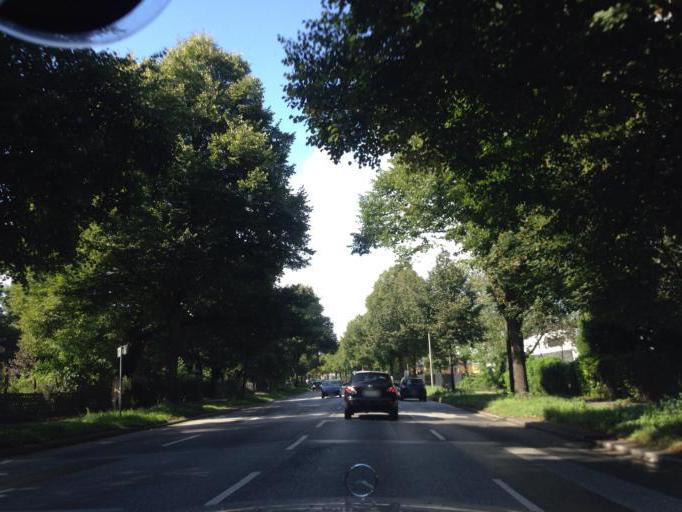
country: DE
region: Hamburg
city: Steilshoop
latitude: 53.5879
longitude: 10.0630
